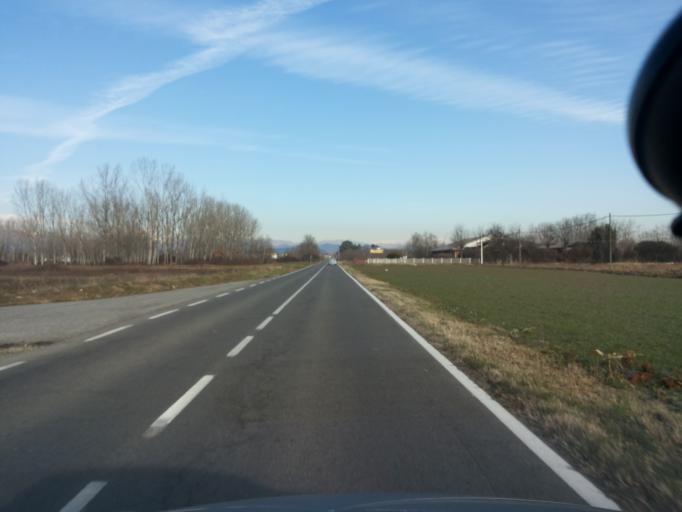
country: IT
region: Piedmont
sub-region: Provincia di Vercelli
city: Ghislarengo
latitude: 45.5158
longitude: 8.3873
